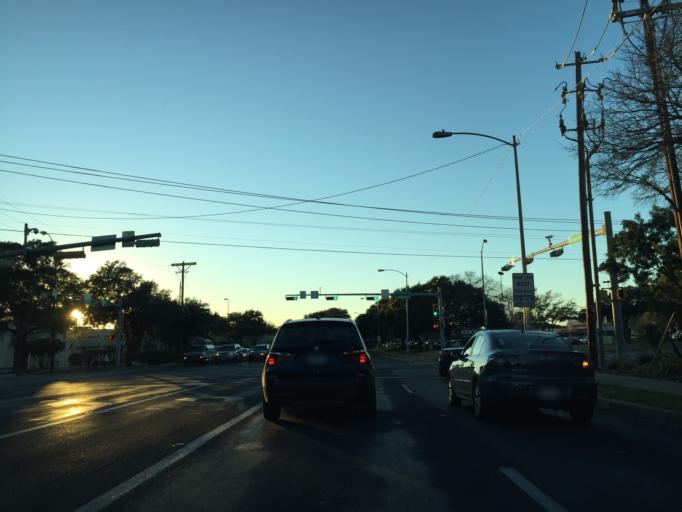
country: US
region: Texas
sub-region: Williamson County
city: Jollyville
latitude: 30.3943
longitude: -97.7493
